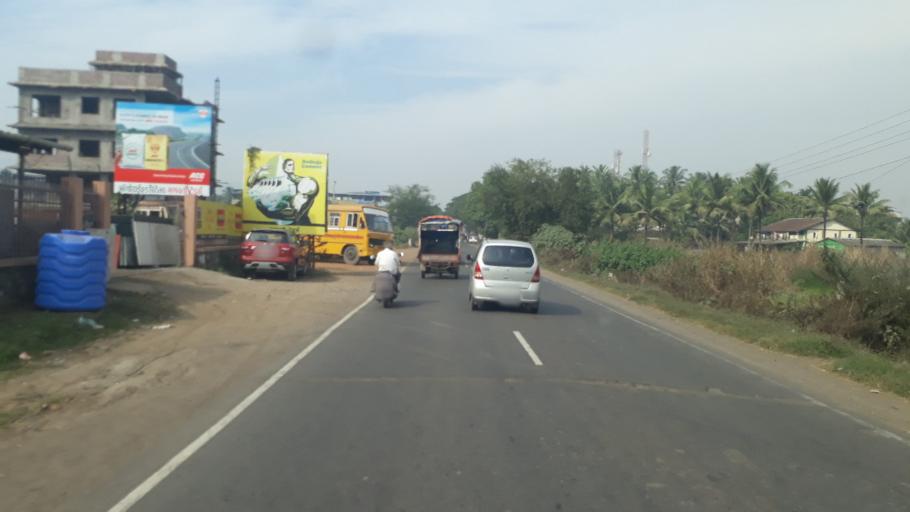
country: IN
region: Maharashtra
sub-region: Raigarh
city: Pen
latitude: 18.6871
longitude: 72.9958
